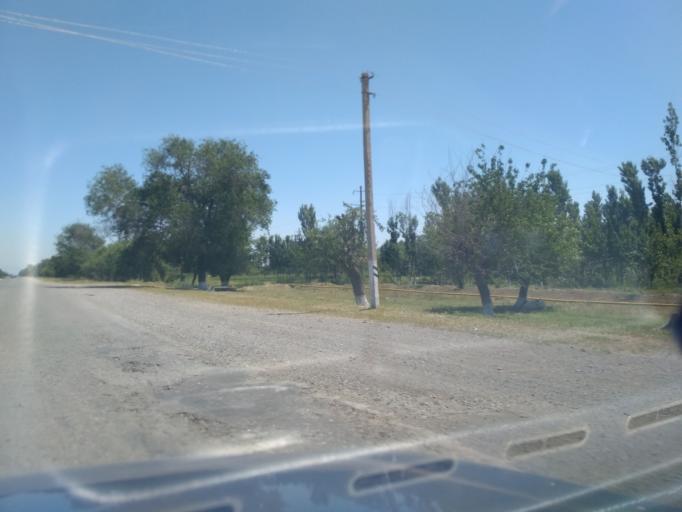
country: TJ
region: Viloyati Sughd
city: Zafarobod
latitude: 40.2224
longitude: 68.9305
